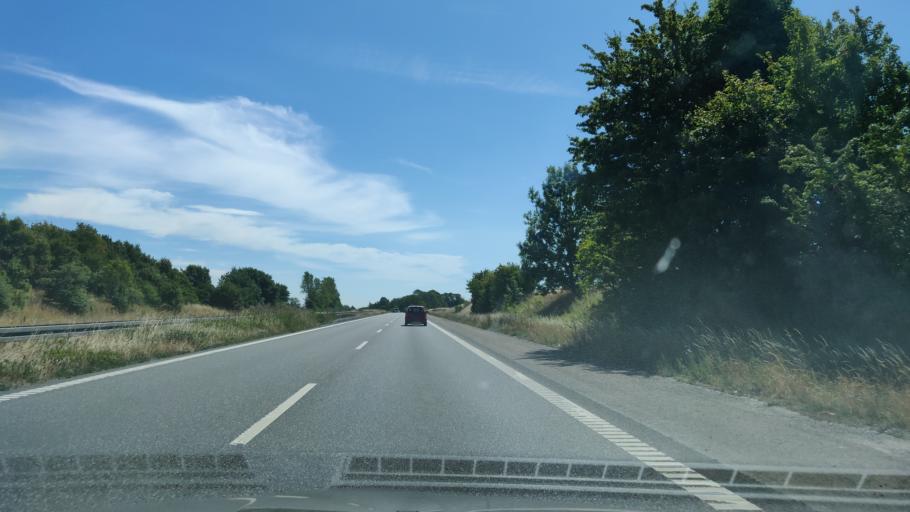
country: DK
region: Zealand
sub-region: Holbaek Kommune
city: Vipperod
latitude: 55.6606
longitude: 11.7615
